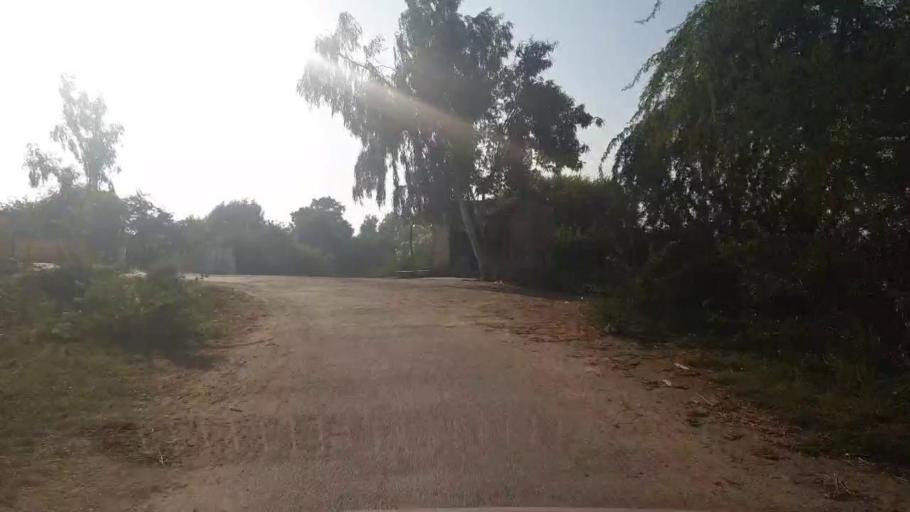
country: PK
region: Sindh
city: Tando Bago
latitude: 24.7346
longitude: 68.9313
